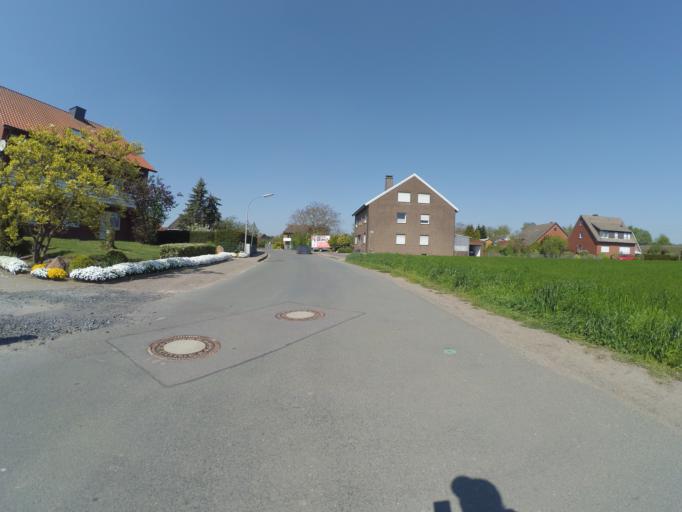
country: DE
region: North Rhine-Westphalia
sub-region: Regierungsbezirk Munster
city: Ascheberg
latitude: 51.8132
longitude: 7.5969
